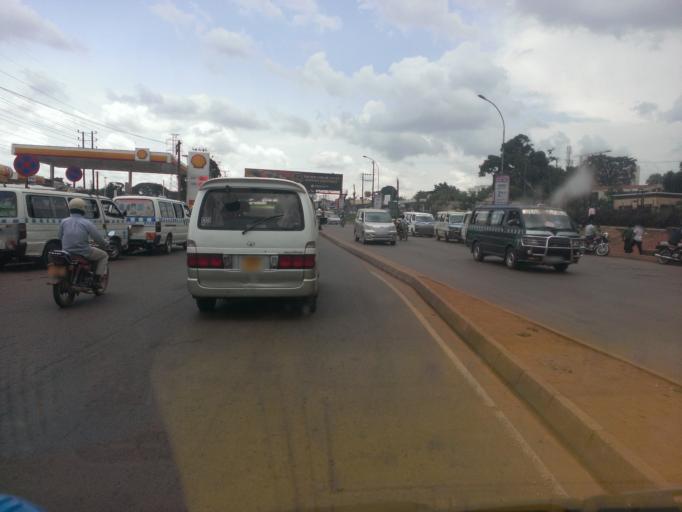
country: UG
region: Central Region
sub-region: Kampala District
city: Kampala
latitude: 0.3285
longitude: 32.6122
